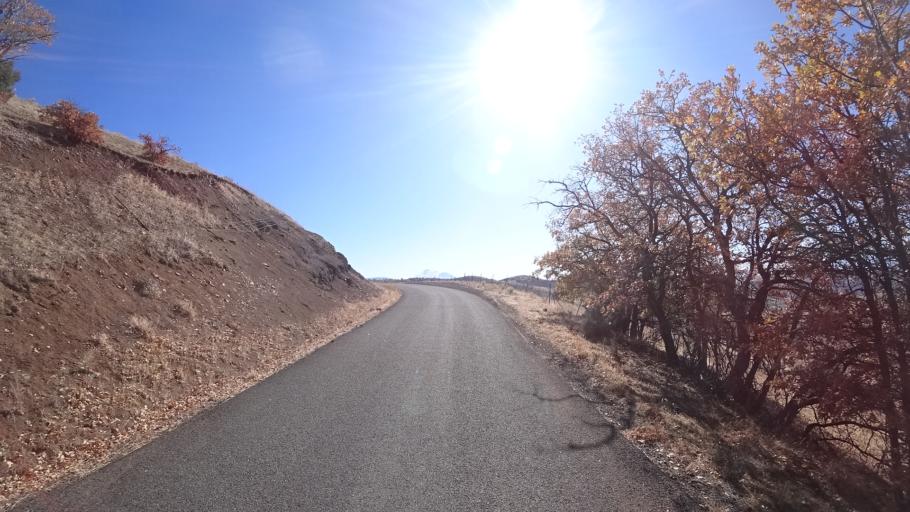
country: US
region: California
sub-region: Siskiyou County
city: Montague
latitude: 41.8244
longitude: -122.3427
